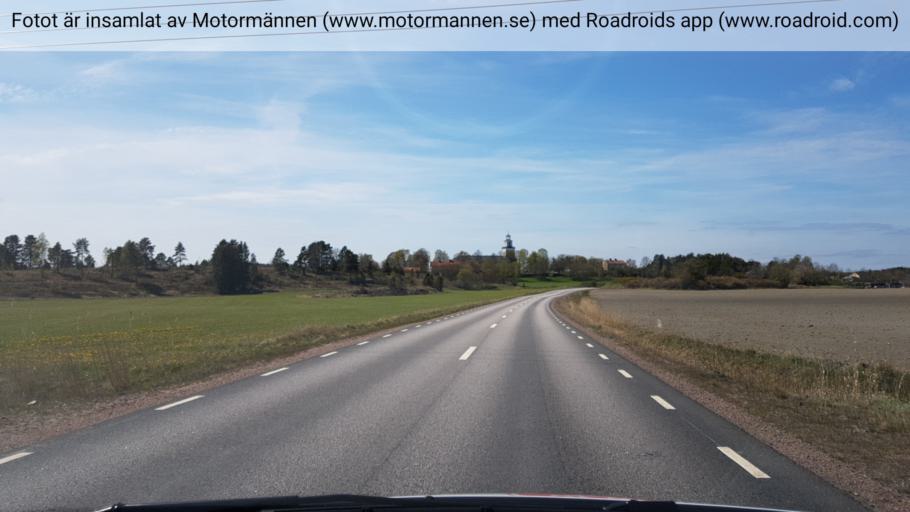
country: SE
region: Kalmar
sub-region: Vasterviks Kommun
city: Forserum
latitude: 57.9383
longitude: 16.4734
